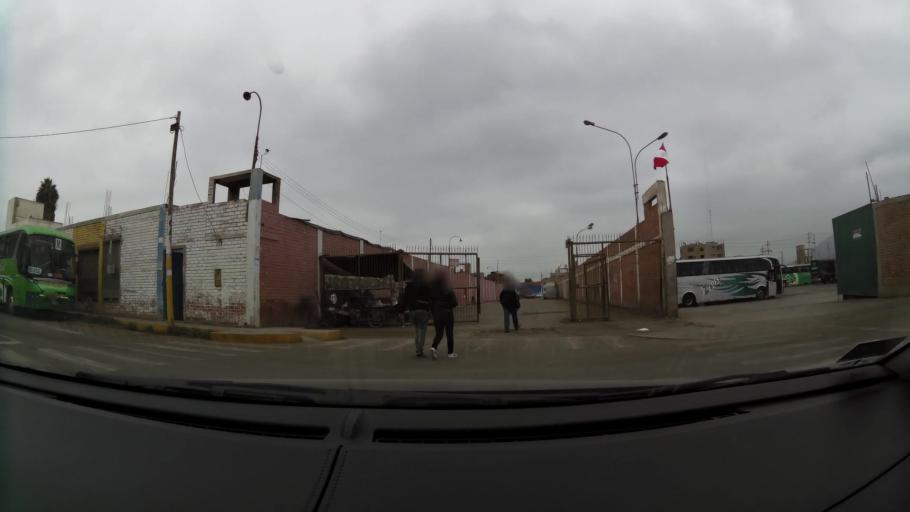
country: PE
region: Lima
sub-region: Provincia de Huaral
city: Huaral
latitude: -11.4998
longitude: -77.2060
